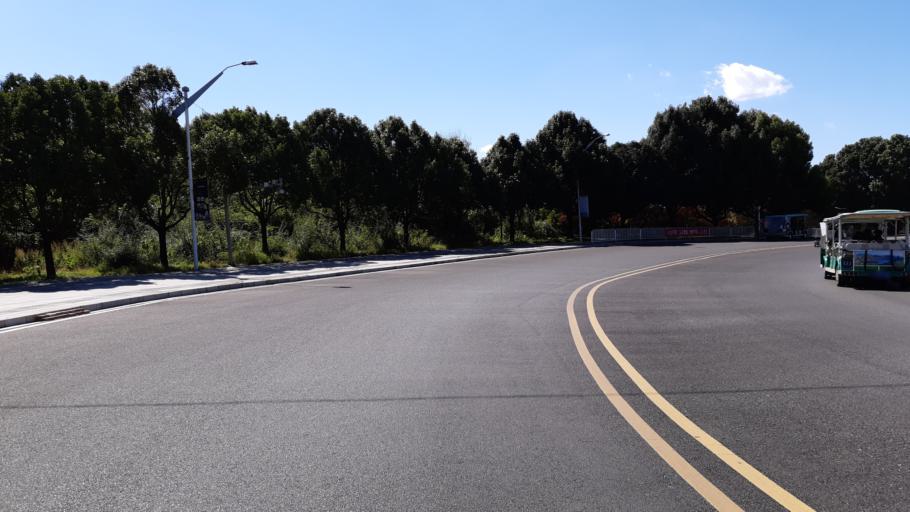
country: CN
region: Yunnan
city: Shilin
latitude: 24.8273
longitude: 103.3247
